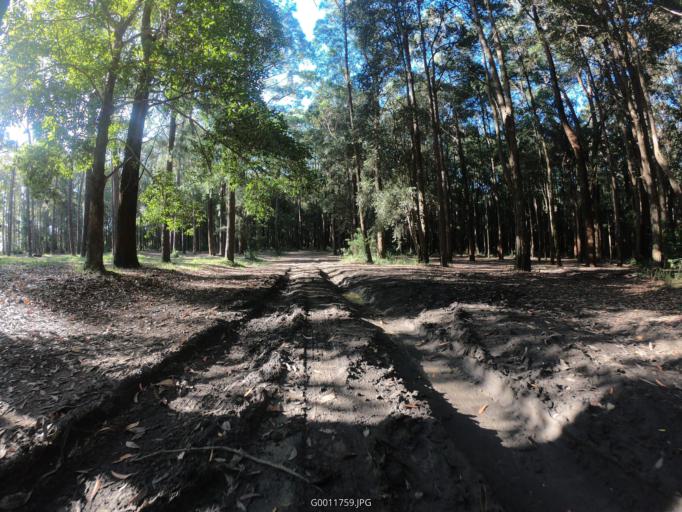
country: AU
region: New South Wales
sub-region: Lake Macquarie Shire
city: Cooranbong
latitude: -33.0624
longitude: 151.3322
